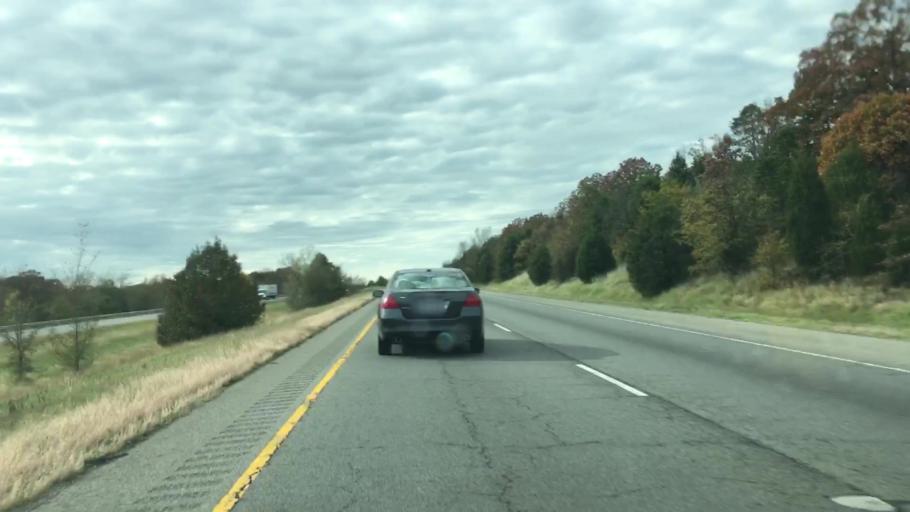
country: US
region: Arkansas
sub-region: Faulkner County
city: Conway
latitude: 35.1218
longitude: -92.4940
